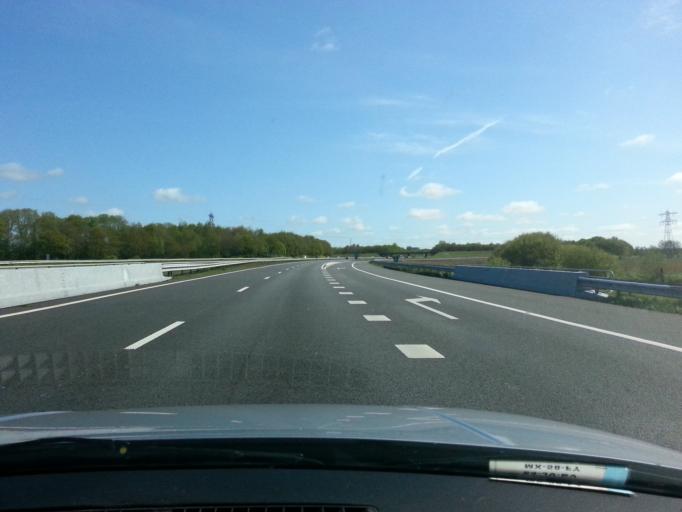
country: NL
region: Friesland
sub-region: Gemeente Smallingerland
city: Boornbergum
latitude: 53.0860
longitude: 6.0777
